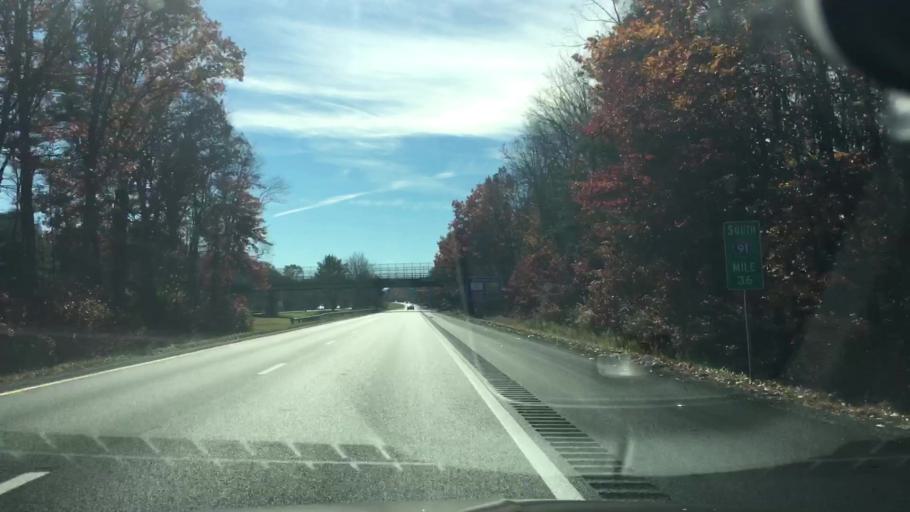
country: US
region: Massachusetts
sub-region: Franklin County
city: South Deerfield
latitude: 42.4856
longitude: -72.6164
